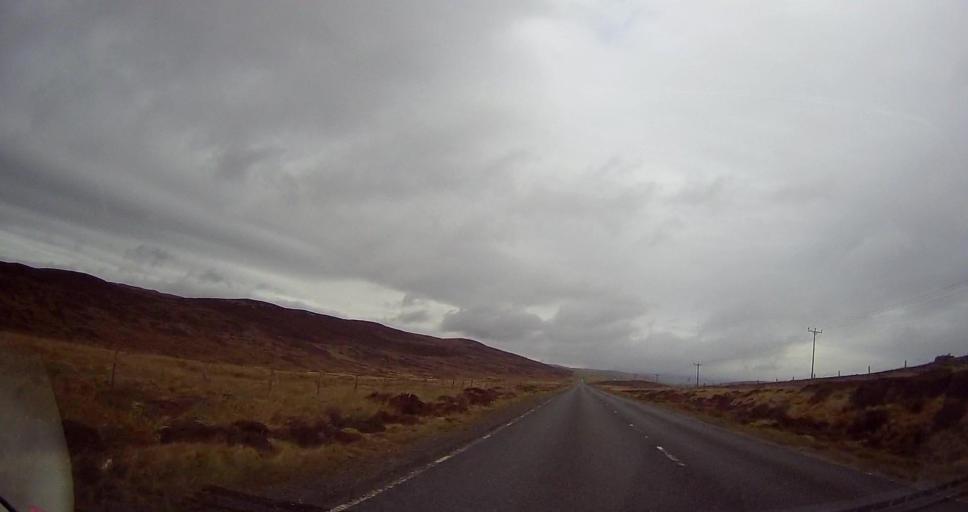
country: GB
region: Scotland
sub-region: Shetland Islands
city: Lerwick
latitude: 60.2051
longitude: -1.2331
